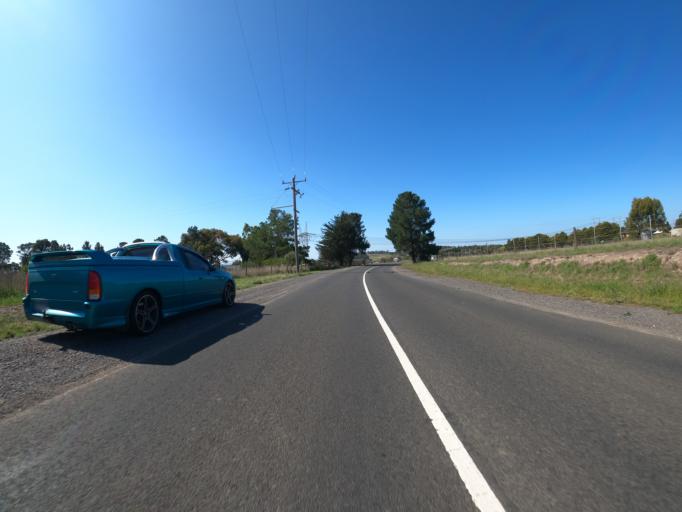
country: AU
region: Victoria
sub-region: Hume
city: Greenvale
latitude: -37.5482
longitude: 144.8690
